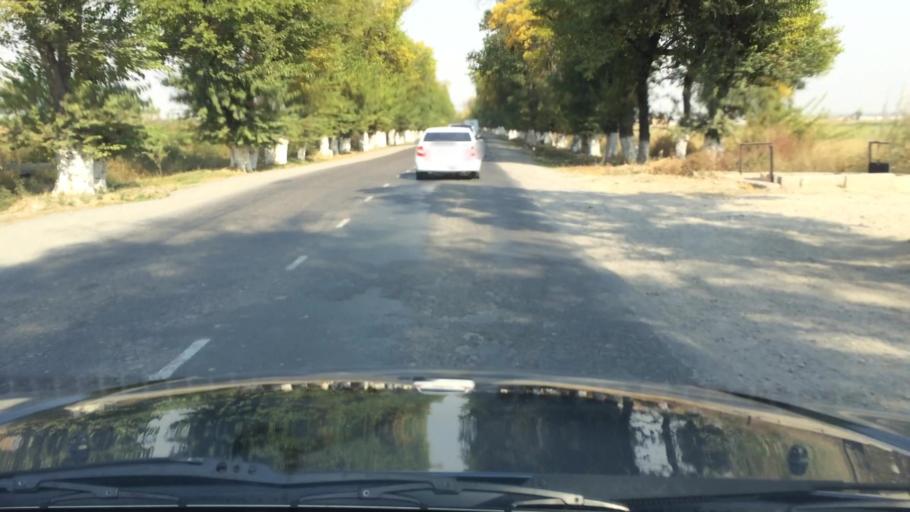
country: KG
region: Chuy
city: Lebedinovka
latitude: 42.9046
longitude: 74.6861
